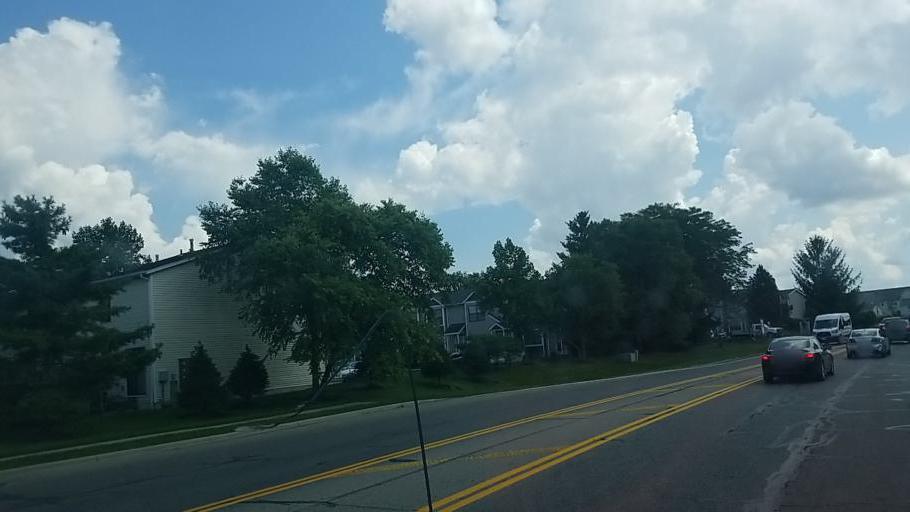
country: US
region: Ohio
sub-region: Franklin County
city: Worthington
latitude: 40.1330
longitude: -82.9911
